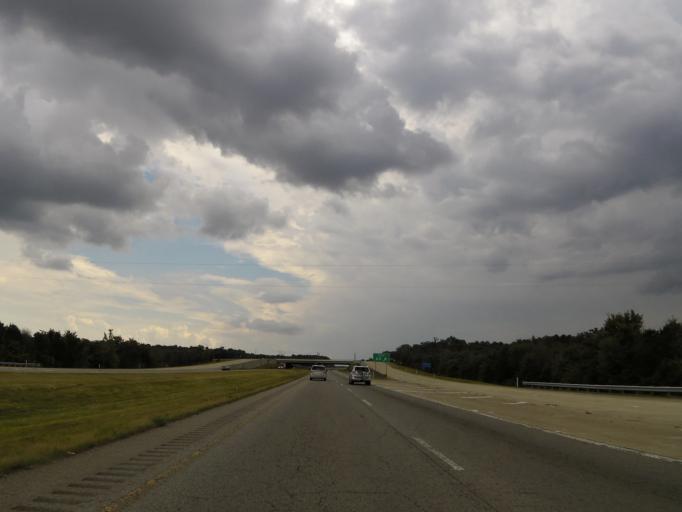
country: US
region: Tennessee
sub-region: Wilson County
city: Rural Hill
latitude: 36.0448
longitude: -86.4300
